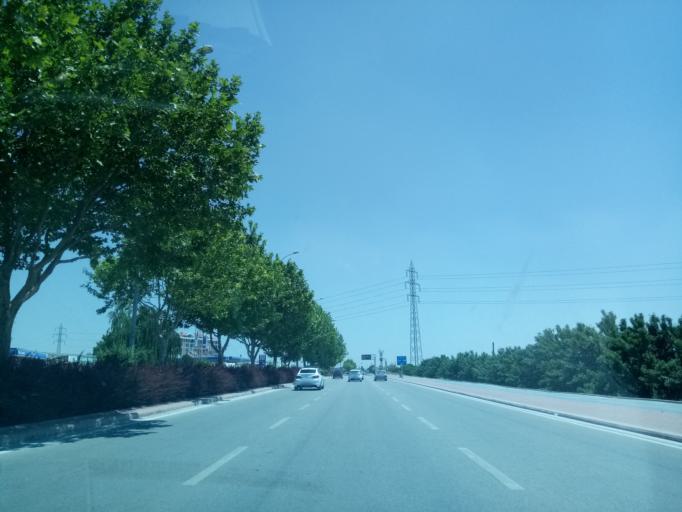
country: TR
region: Konya
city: Meram
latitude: 37.8271
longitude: 32.4734
